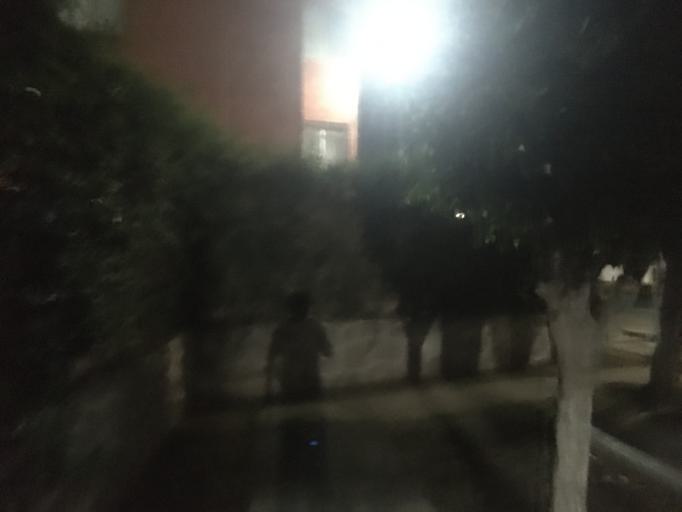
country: MX
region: Queretaro
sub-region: Queretaro
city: Santiago de Queretaro
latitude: 20.6117
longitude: -100.4034
